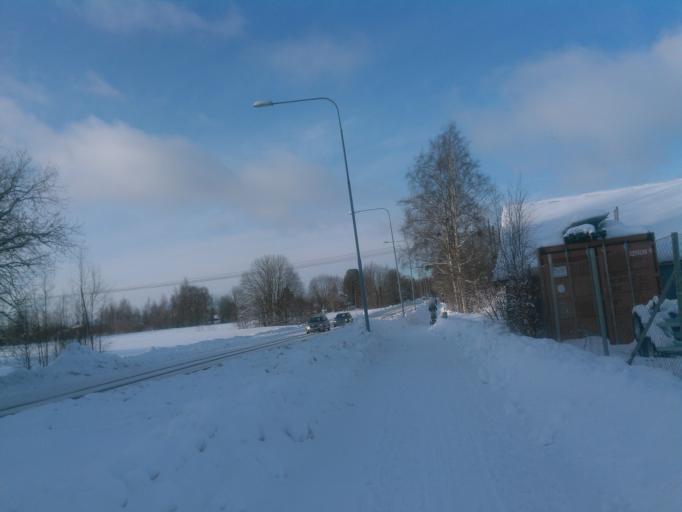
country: SE
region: Vaesterbotten
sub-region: Umea Kommun
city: Umea
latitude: 63.8077
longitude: 20.2726
